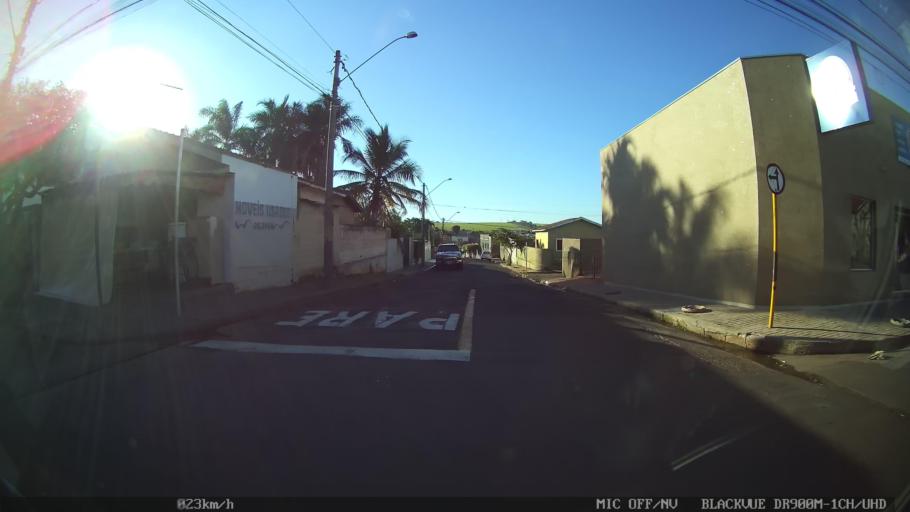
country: BR
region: Sao Paulo
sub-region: Guapiacu
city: Guapiacu
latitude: -20.7943
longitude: -49.2245
